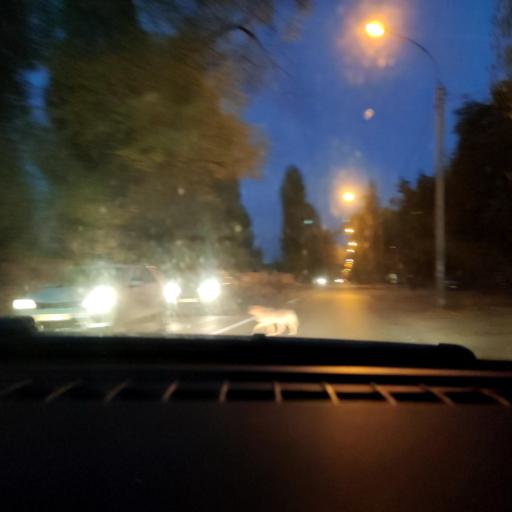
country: RU
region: Voronezj
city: Maslovka
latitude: 51.6098
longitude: 39.2377
